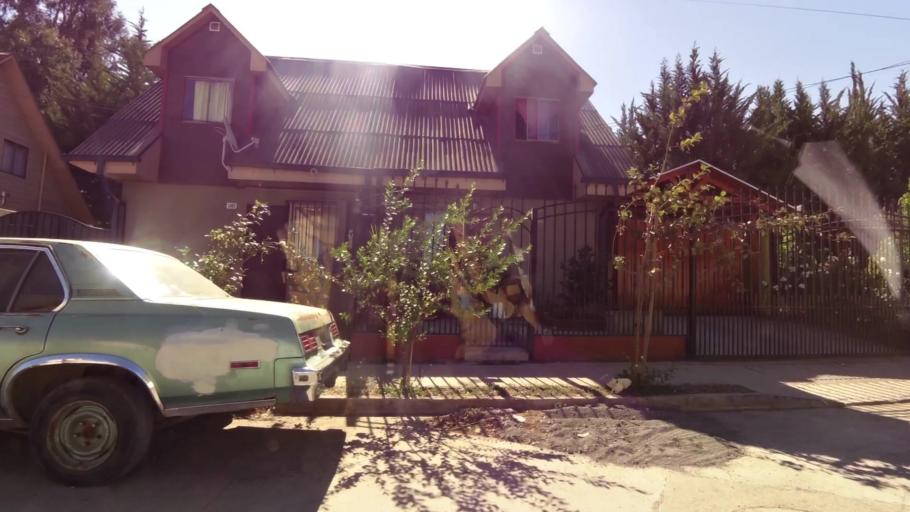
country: CL
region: Maule
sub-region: Provincia de Talca
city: Talca
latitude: -35.4089
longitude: -71.6204
